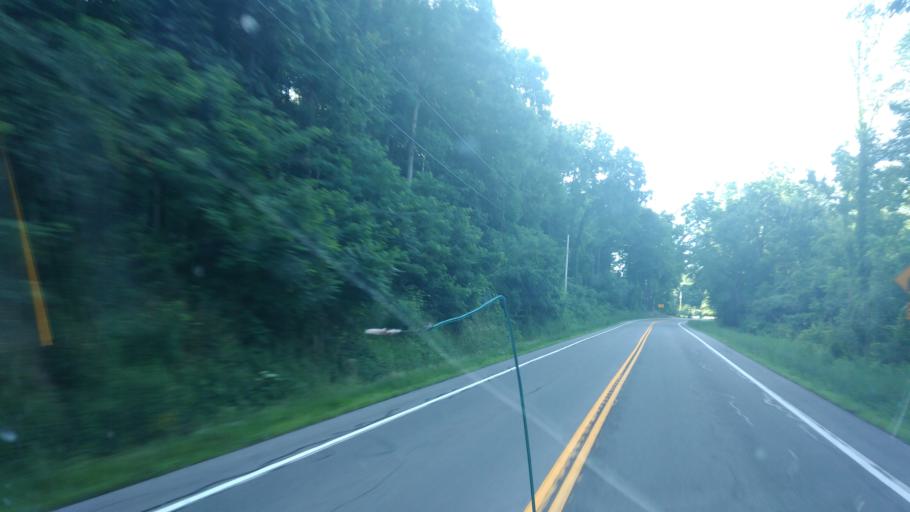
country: US
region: New York
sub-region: Wayne County
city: Lyons
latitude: 43.0884
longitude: -76.9861
